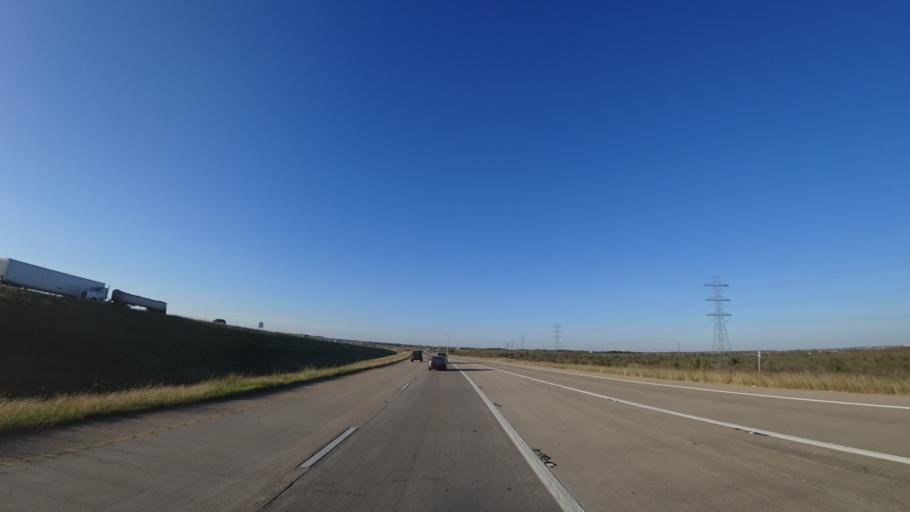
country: US
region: Texas
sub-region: Travis County
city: Garfield
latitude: 30.1236
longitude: -97.6607
